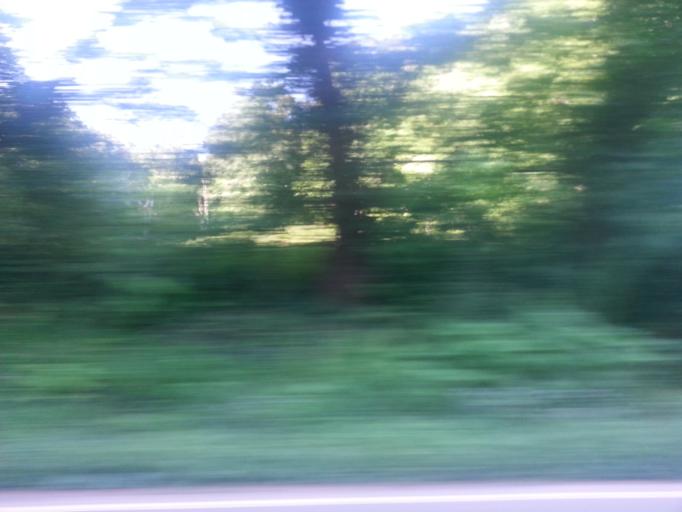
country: US
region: Tennessee
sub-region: Blount County
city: Maryville
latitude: 35.6655
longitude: -83.9640
